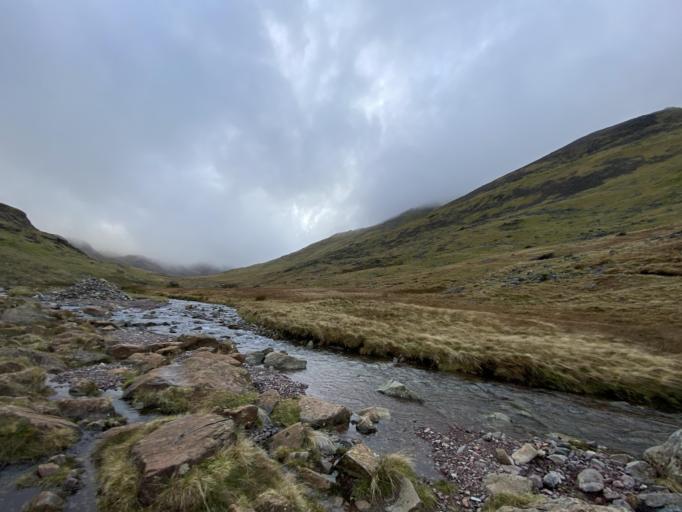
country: GB
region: England
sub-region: Cumbria
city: Keswick
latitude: 54.4824
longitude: -3.1997
